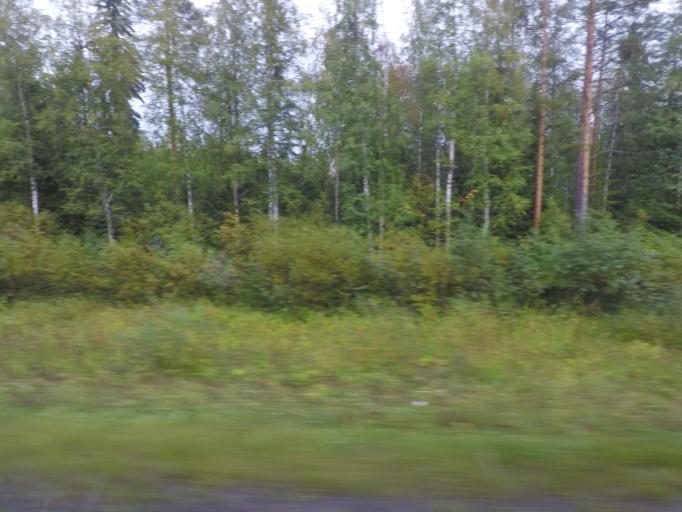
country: FI
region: Southern Savonia
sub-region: Pieksaemaeki
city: Juva
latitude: 61.9263
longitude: 27.8073
